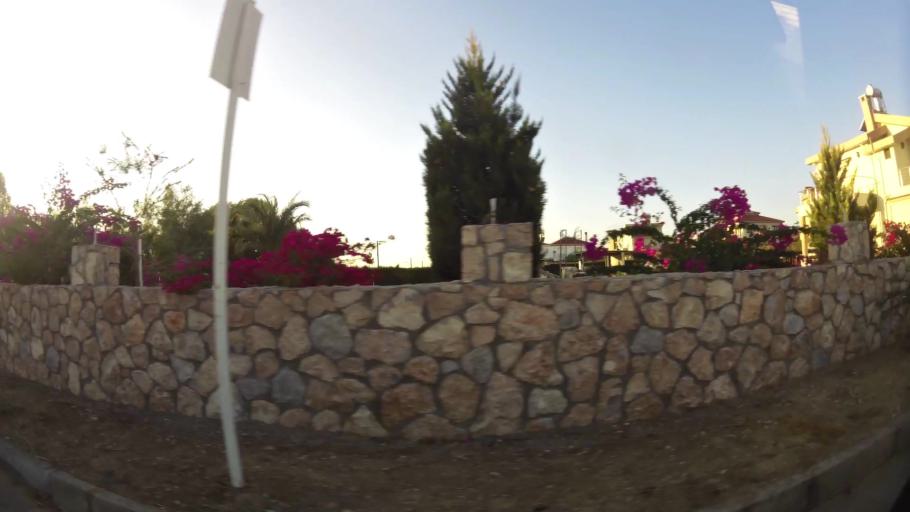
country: CY
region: Lefkosia
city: Nicosia
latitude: 35.1916
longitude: 33.3184
